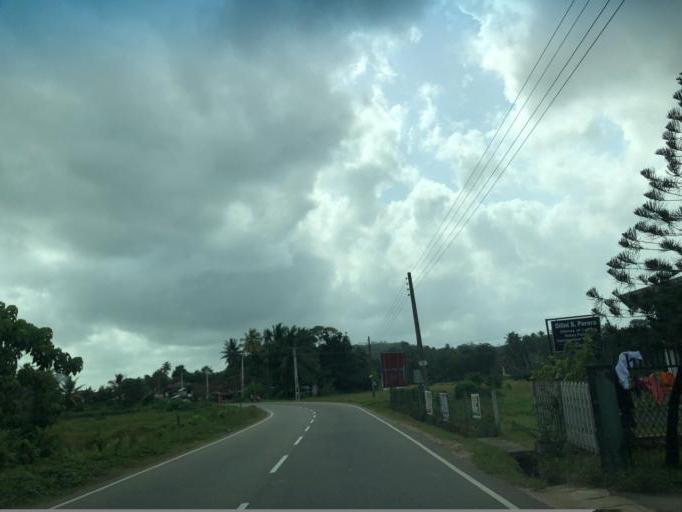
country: LK
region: Western
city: Horana South
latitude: 6.6746
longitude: 80.1205
